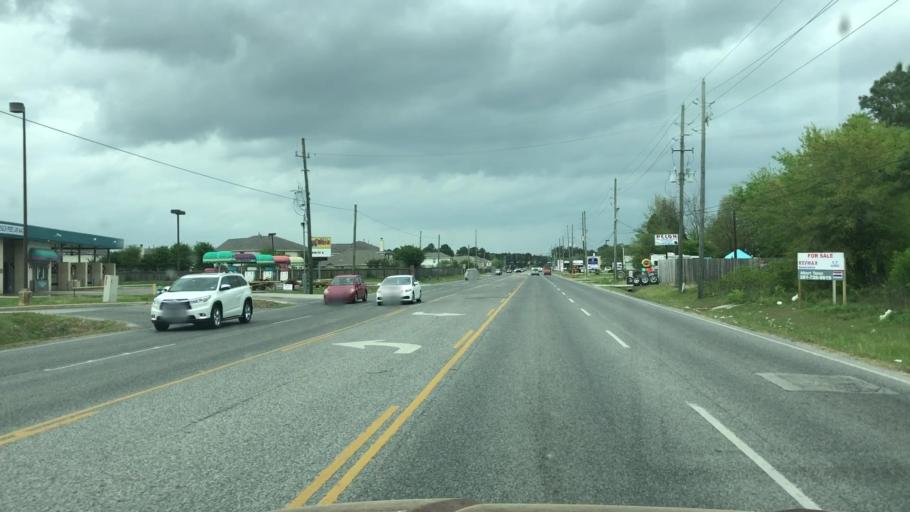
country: US
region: Texas
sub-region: Harris County
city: Spring
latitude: 30.0527
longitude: -95.4937
